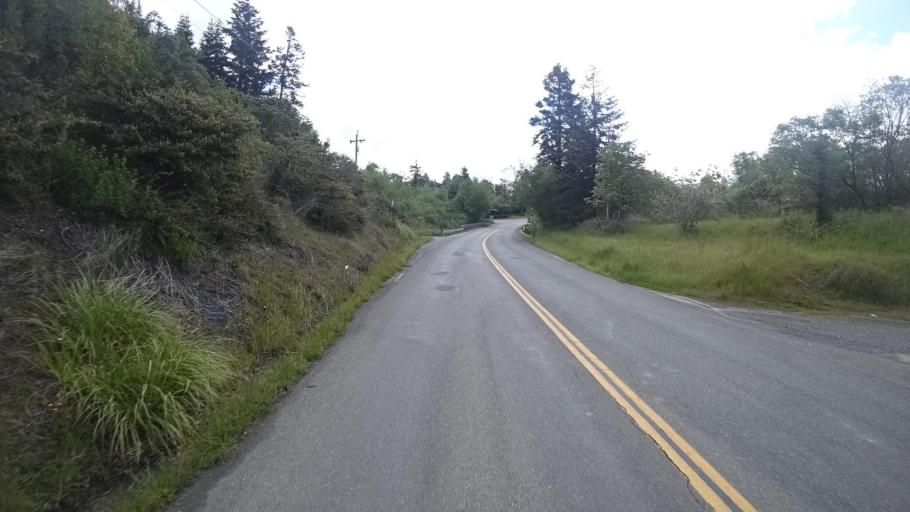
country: US
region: California
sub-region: Humboldt County
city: Blue Lake
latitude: 40.9032
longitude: -124.0304
